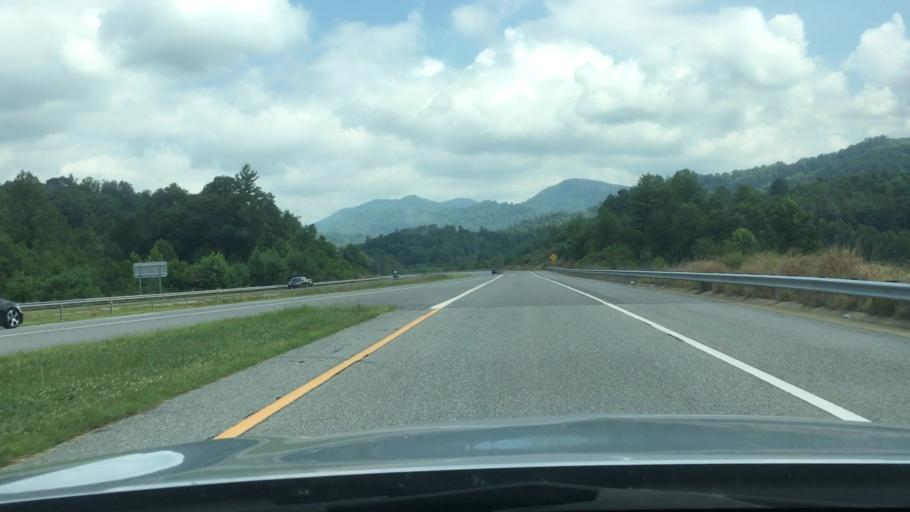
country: US
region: North Carolina
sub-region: Madison County
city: Mars Hill
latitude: 35.8417
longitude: -82.5230
